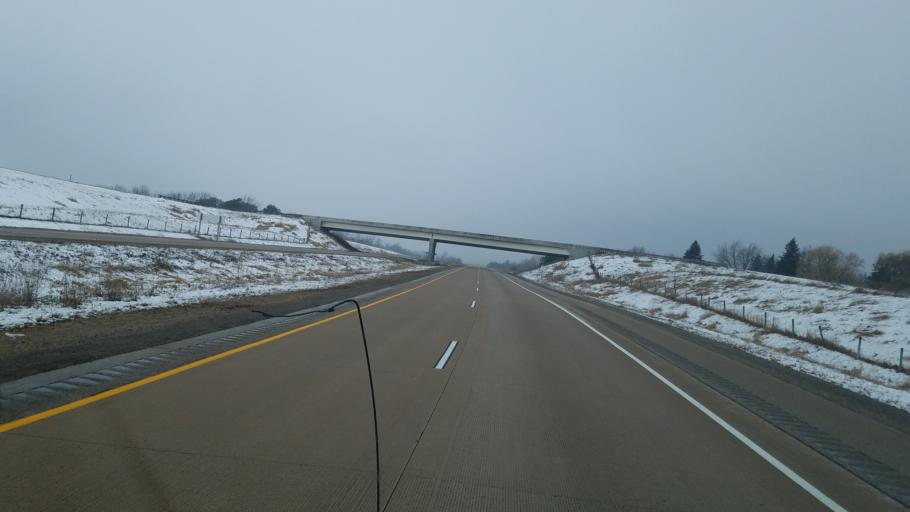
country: US
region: Wisconsin
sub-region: Winnebago County
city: Winneconne
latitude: 44.1824
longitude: -88.6653
